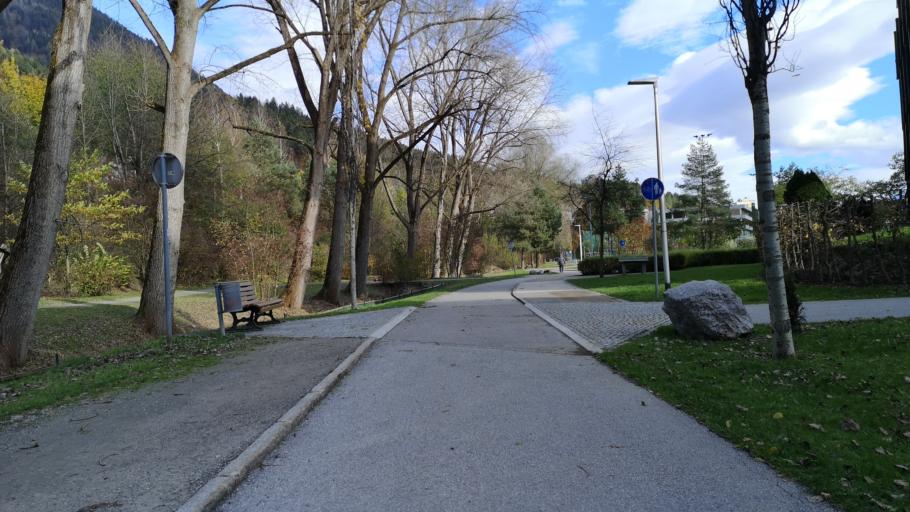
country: AT
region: Tyrol
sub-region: Politischer Bezirk Innsbruck Land
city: Vols
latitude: 47.2668
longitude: 11.3410
